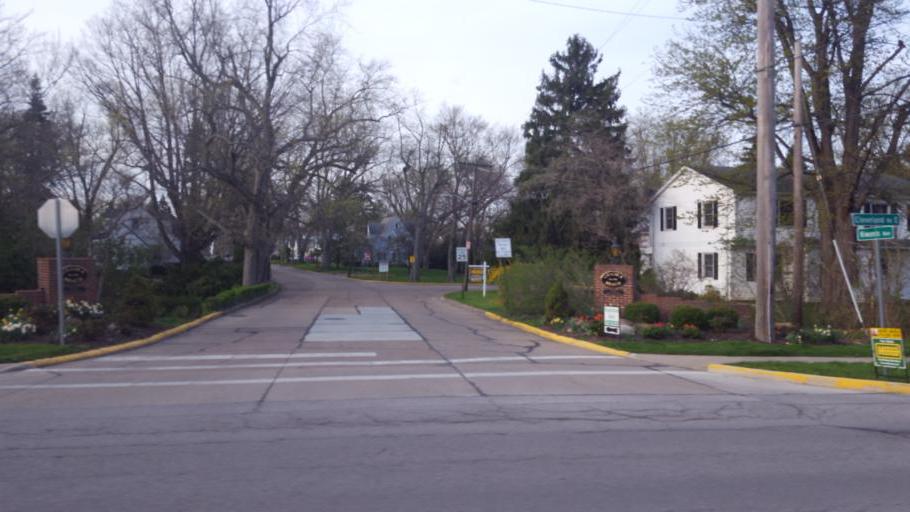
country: US
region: Ohio
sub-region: Erie County
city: Huron
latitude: 41.3883
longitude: -82.5379
